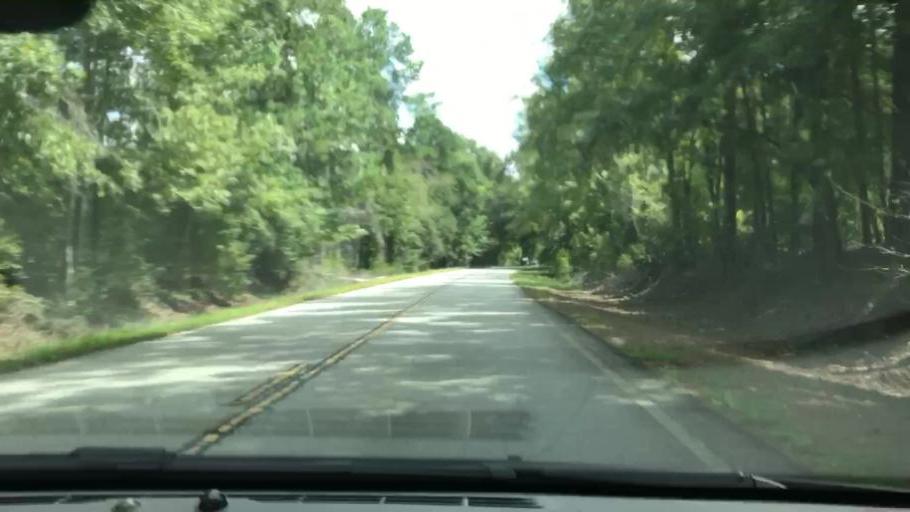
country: US
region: Georgia
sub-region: Quitman County
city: Georgetown
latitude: 32.0401
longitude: -85.0302
